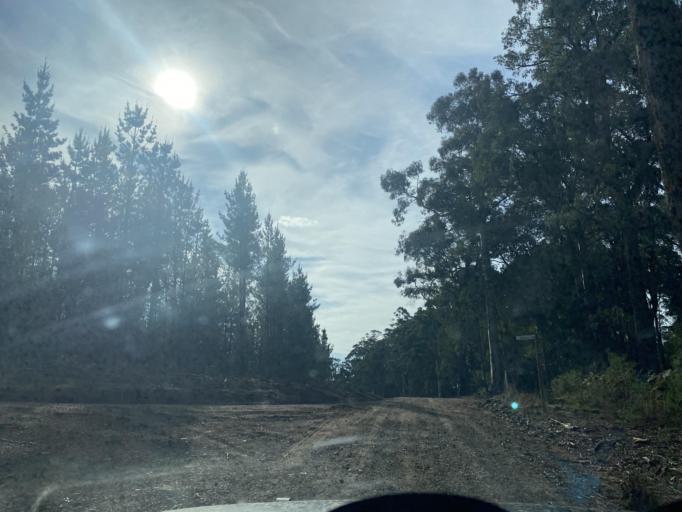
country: AU
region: Victoria
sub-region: Mansfield
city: Mansfield
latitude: -36.8836
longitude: 146.1957
